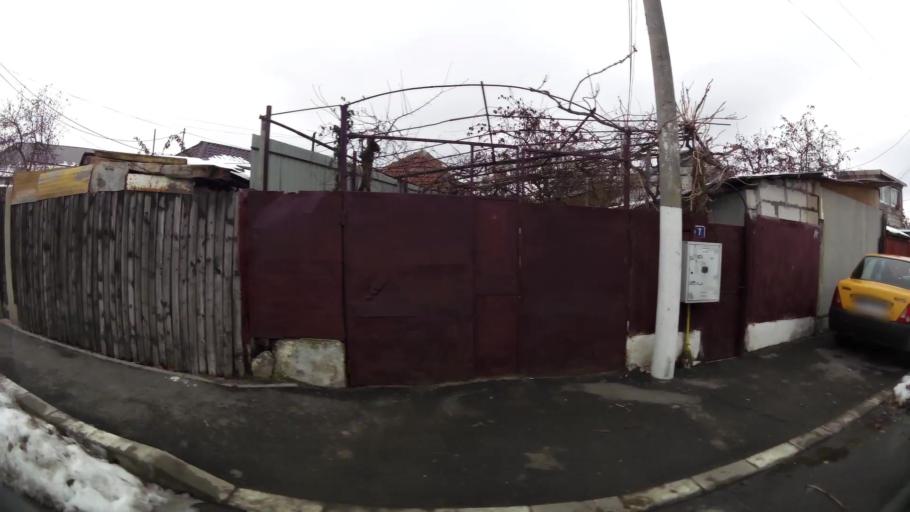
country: RO
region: Ilfov
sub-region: Comuna Pantelimon
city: Pantelimon
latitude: 44.4502
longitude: 26.2000
